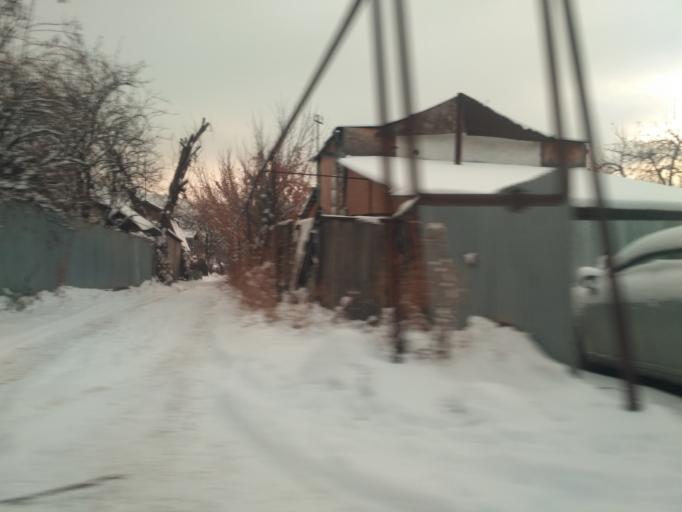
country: KZ
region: Almaty Qalasy
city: Almaty
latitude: 43.2121
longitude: 76.7779
